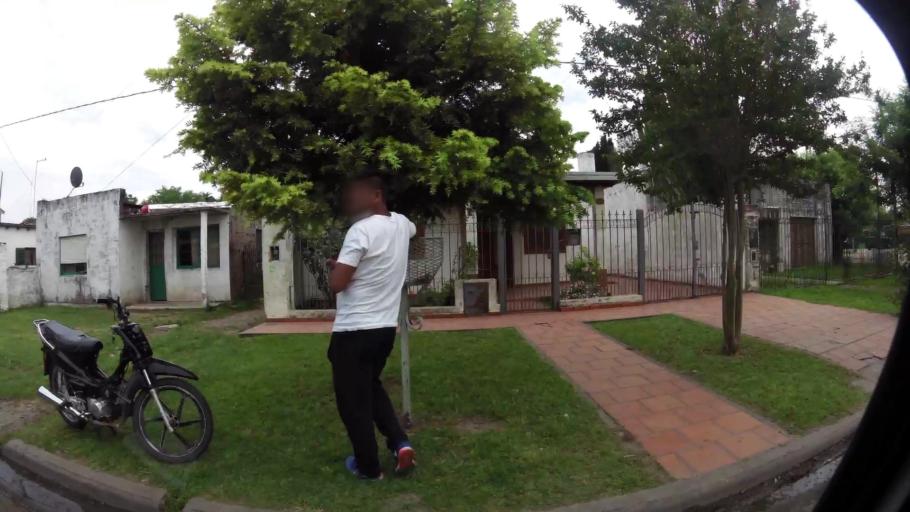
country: AR
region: Buenos Aires
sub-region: Partido de La Plata
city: La Plata
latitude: -34.9189
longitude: -58.0118
